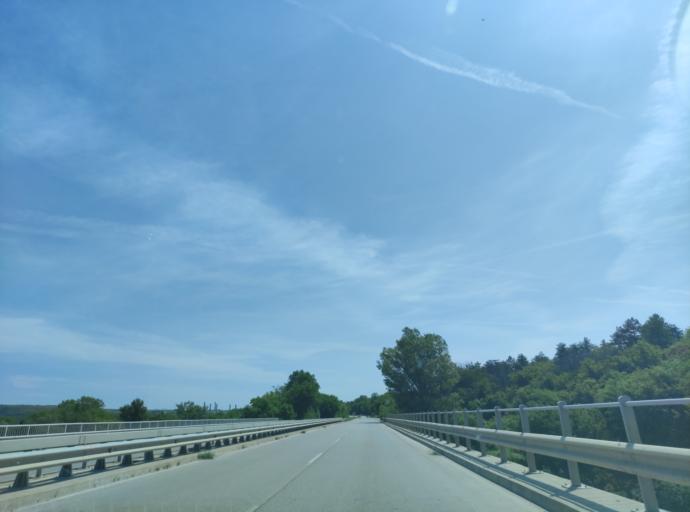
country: BG
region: Pleven
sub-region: Obshtina Dolna Mitropoliya
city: Dolna Mitropoliya
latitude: 43.4331
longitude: 24.5491
